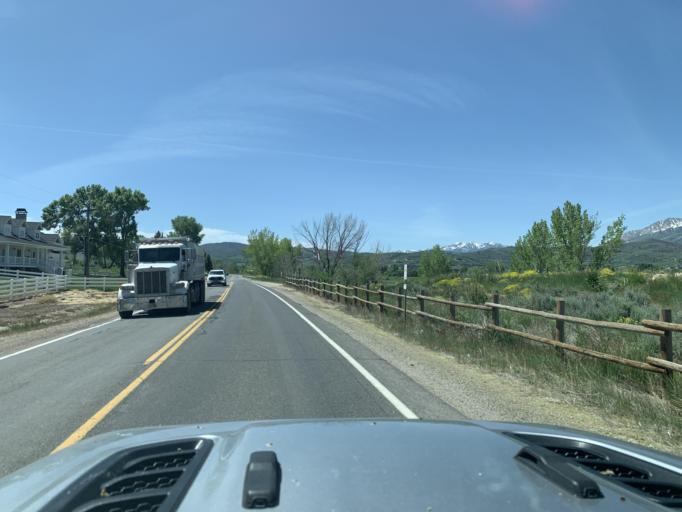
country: US
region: Utah
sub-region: Weber County
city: Wolf Creek
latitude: 41.2723
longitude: -111.7771
